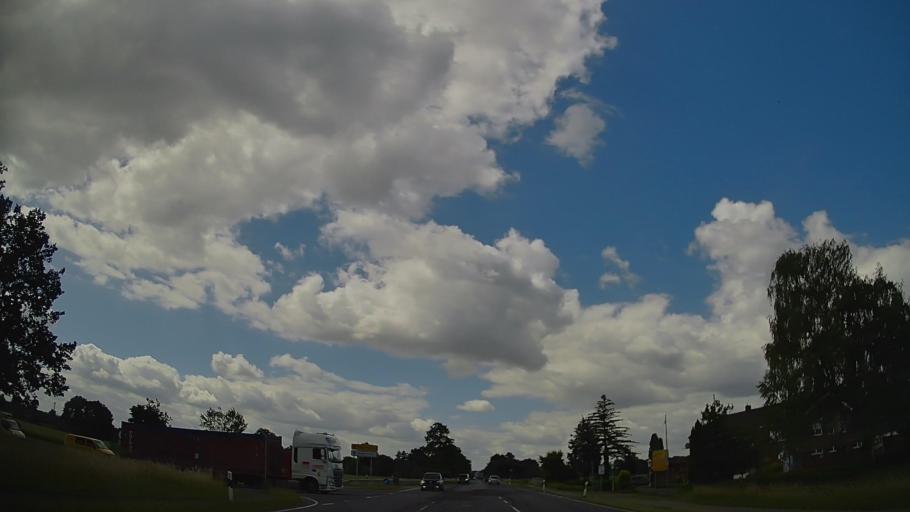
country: DE
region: Lower Saxony
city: Huede
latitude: 52.5078
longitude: 8.3748
